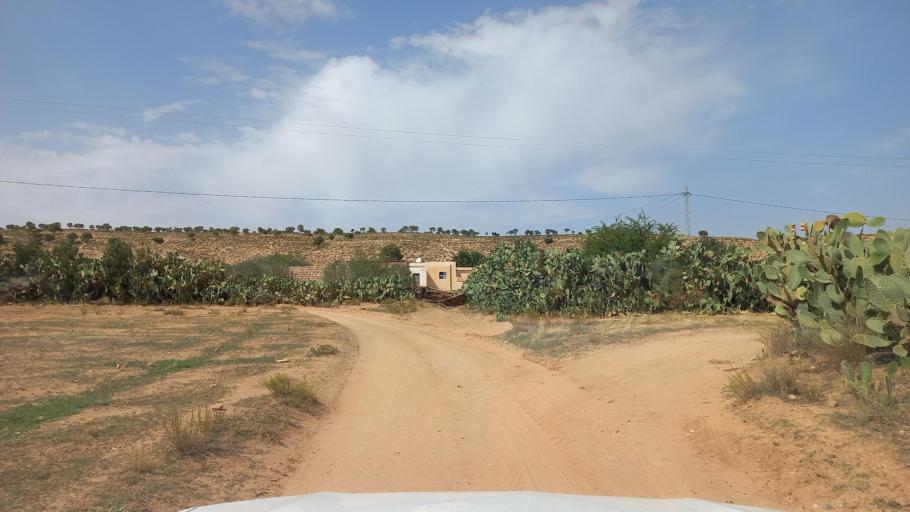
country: TN
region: Al Qasrayn
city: Kasserine
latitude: 35.3703
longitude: 8.8799
